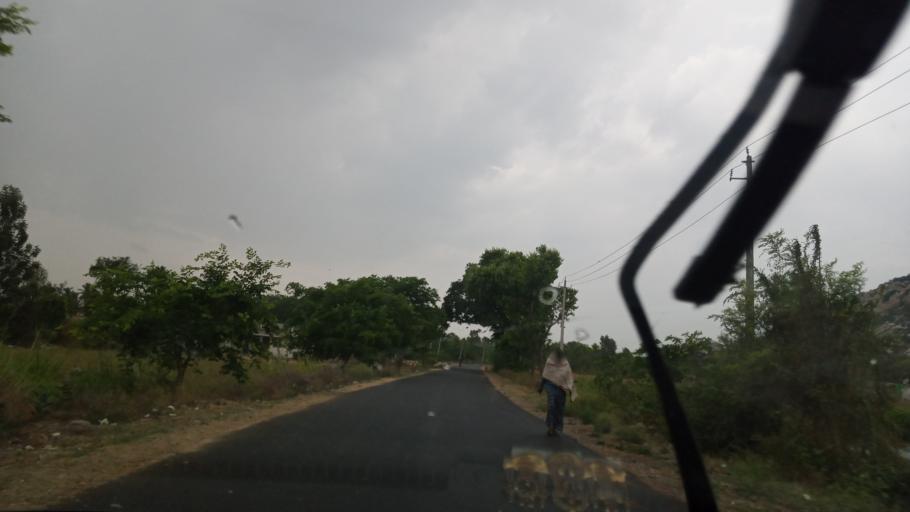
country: IN
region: Karnataka
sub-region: Kolar
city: Mulbagal
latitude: 13.1047
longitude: 78.3258
